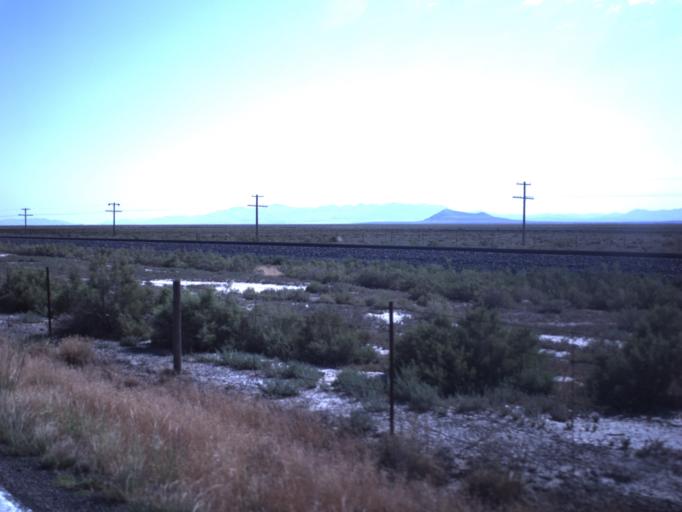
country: US
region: Utah
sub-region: Millard County
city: Delta
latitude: 39.0388
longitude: -112.7721
